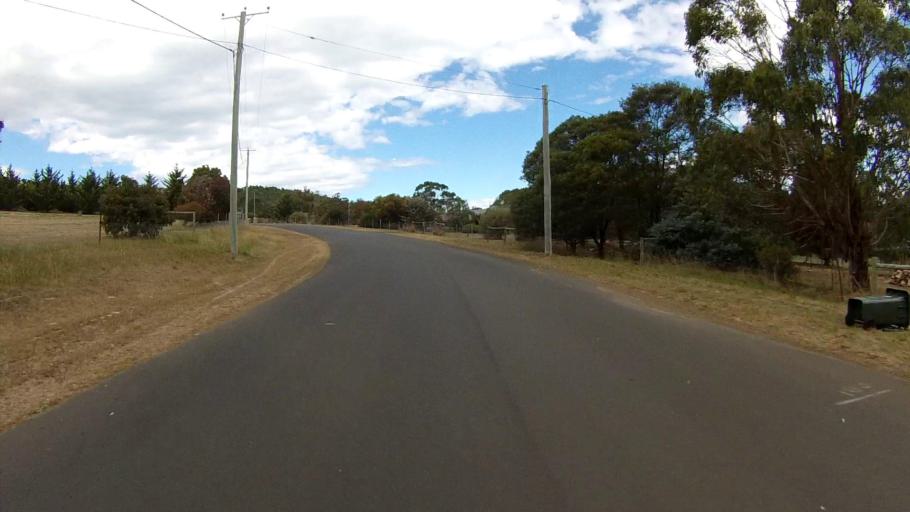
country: AU
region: Tasmania
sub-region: Clarence
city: Acton Park
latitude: -42.8779
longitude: 147.4920
